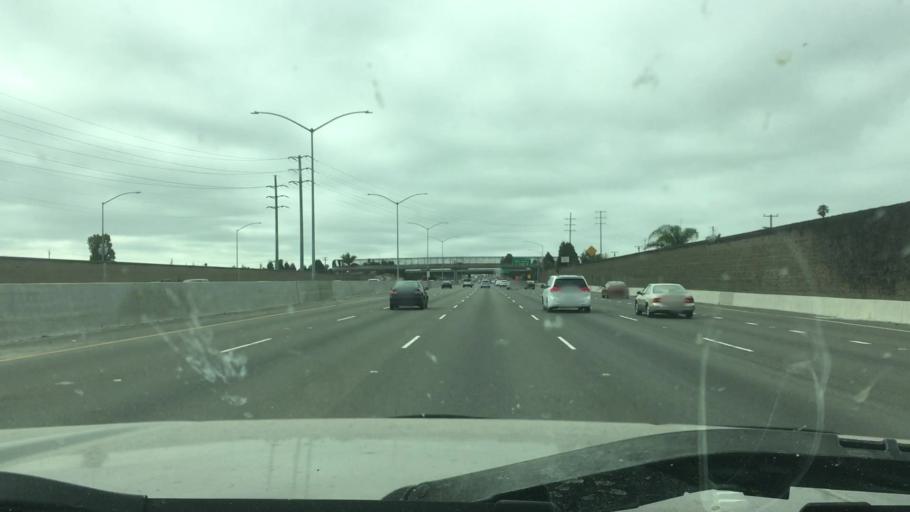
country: US
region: California
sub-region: Alameda County
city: San Leandro
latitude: 37.7361
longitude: -122.1925
